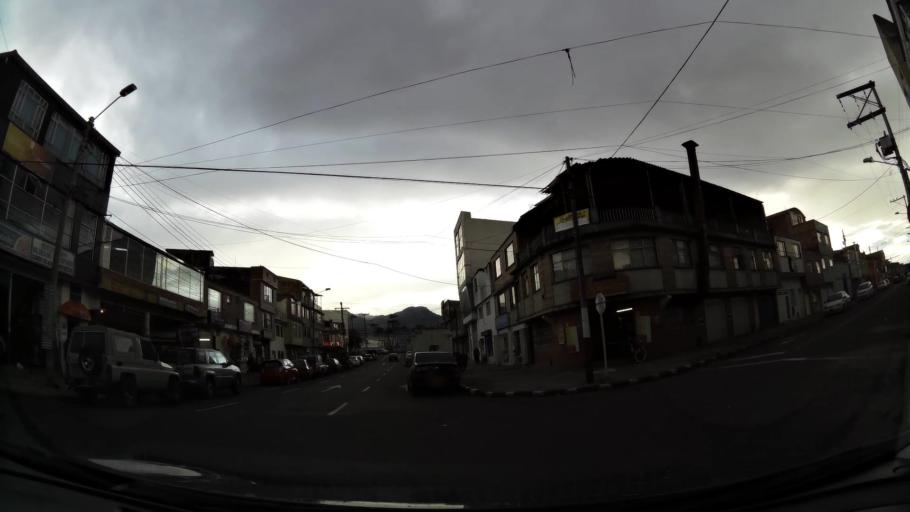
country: CO
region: Bogota D.C.
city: Barrio San Luis
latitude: 4.6763
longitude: -74.0732
